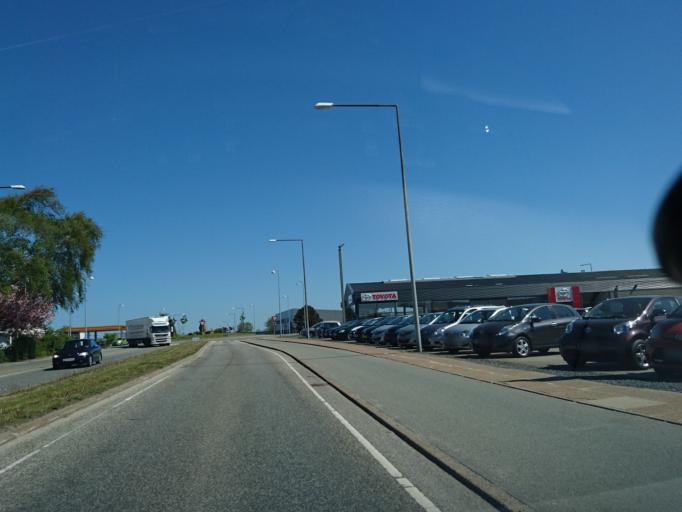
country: DK
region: North Denmark
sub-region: Hjorring Kommune
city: Hjorring
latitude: 57.4484
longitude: 10.0093
